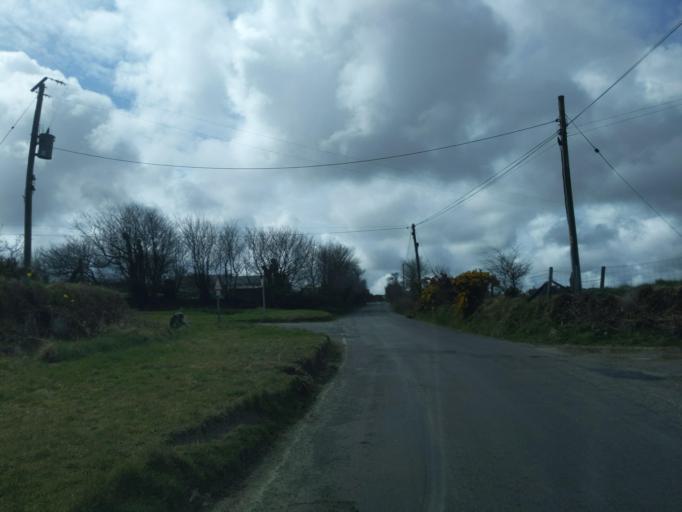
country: GB
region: England
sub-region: Cornwall
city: Camelford
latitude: 50.6245
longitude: -4.5864
